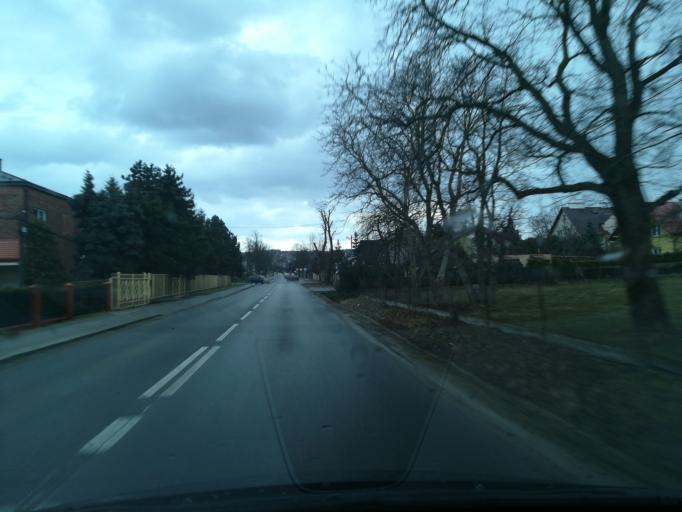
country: PL
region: Subcarpathian Voivodeship
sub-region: Powiat rzeszowski
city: Krasne
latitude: 50.0217
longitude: 22.0499
